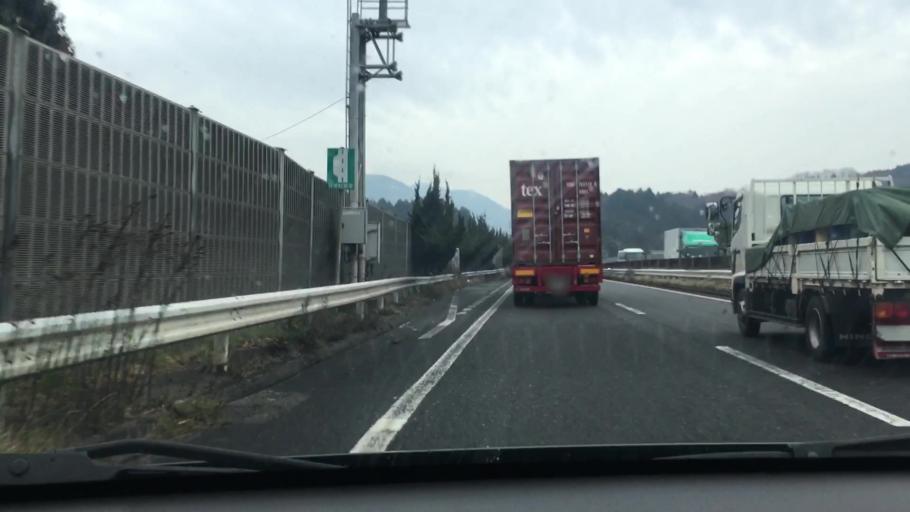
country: JP
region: Mie
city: Ueno-ebisumachi
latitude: 34.8335
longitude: 136.2432
